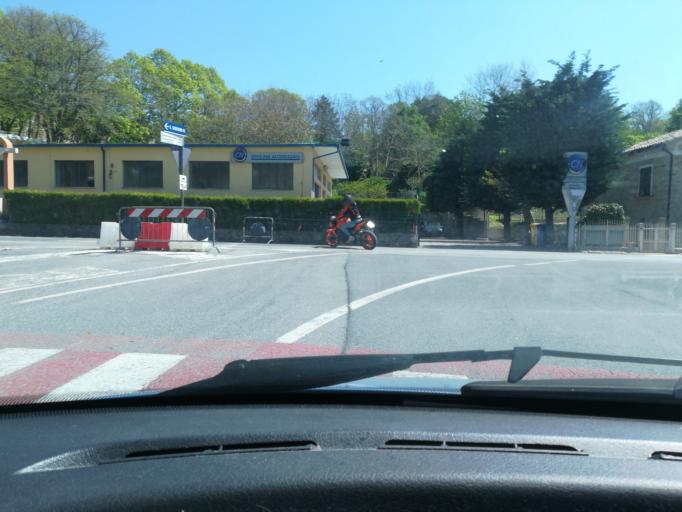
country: IT
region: The Marches
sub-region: Provincia di Macerata
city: Cingoli
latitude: 43.3758
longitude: 13.2130
